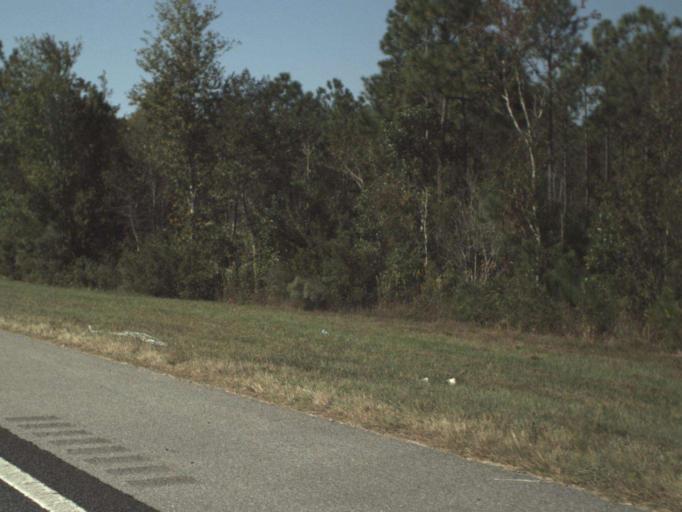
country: US
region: Florida
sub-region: Santa Rosa County
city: Bagdad
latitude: 30.5587
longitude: -87.0463
